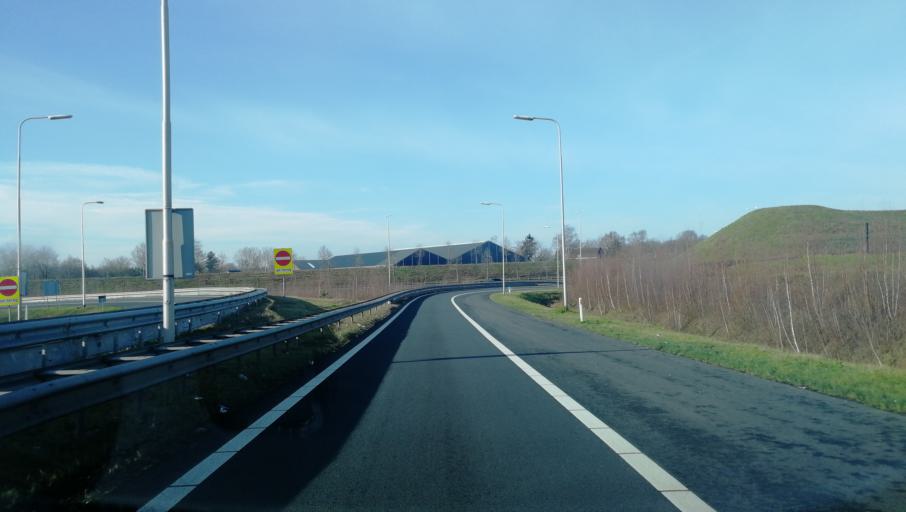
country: NL
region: Limburg
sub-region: Gemeente Venlo
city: Tegelen
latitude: 51.3686
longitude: 6.1251
